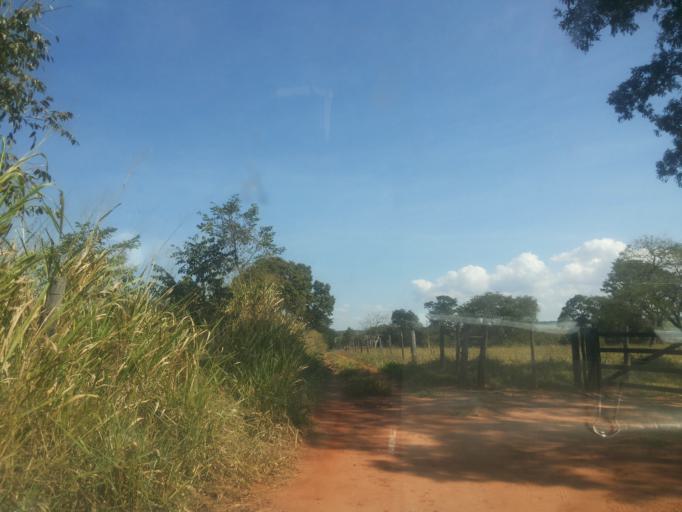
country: BR
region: Minas Gerais
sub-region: Santa Vitoria
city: Santa Vitoria
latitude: -18.9946
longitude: -50.3760
